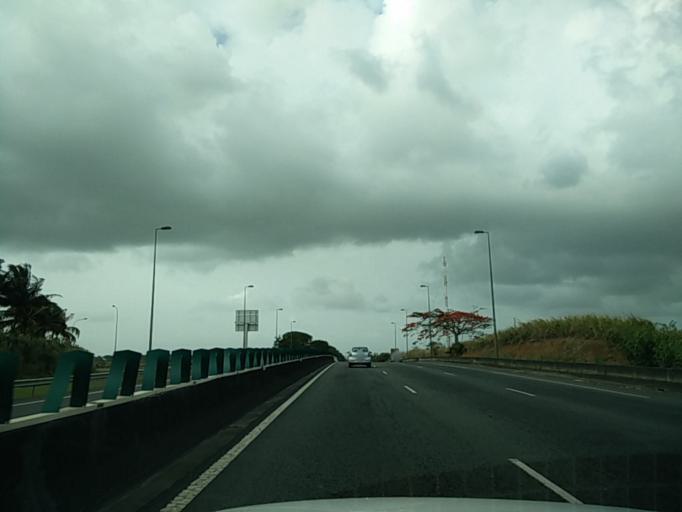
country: GP
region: Guadeloupe
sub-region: Guadeloupe
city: Petit-Bourg
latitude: 16.2204
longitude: -61.5976
